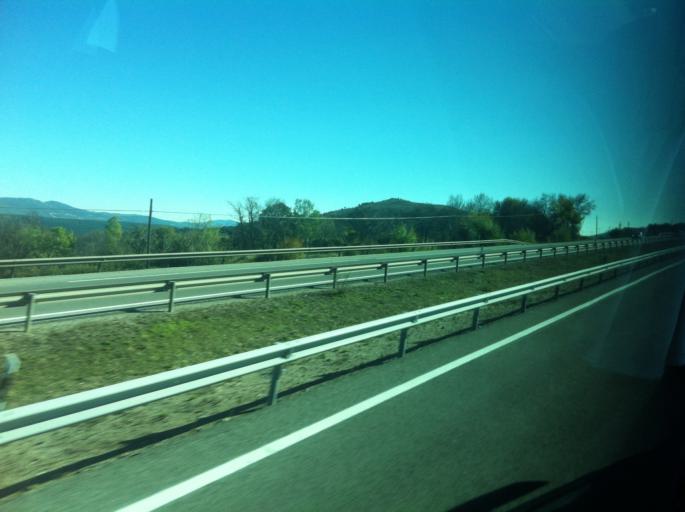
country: ES
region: Madrid
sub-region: Provincia de Madrid
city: Braojos
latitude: 41.0443
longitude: -3.6164
